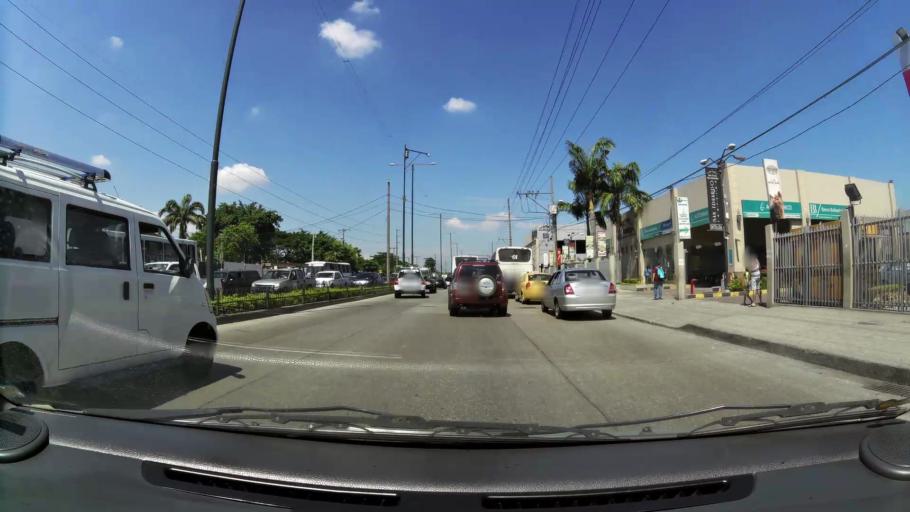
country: EC
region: Guayas
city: Guayaquil
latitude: -2.1900
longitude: -79.9428
